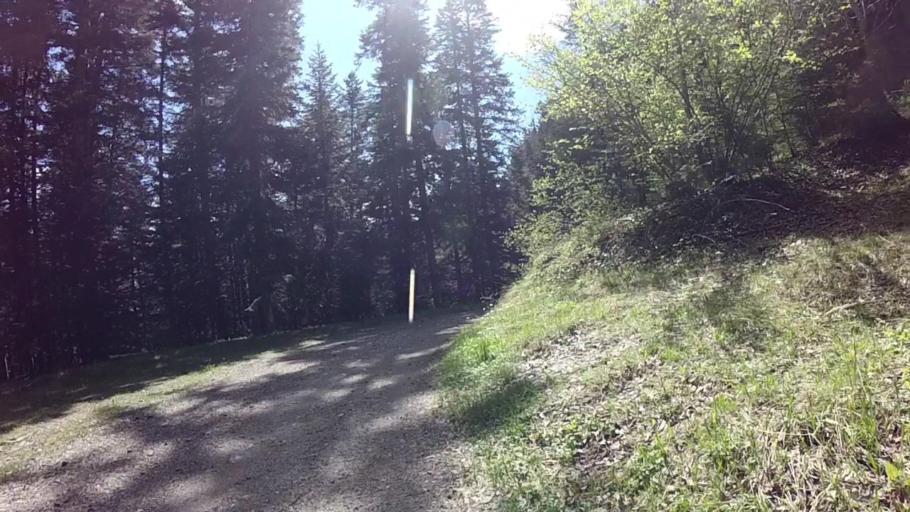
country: FR
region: Provence-Alpes-Cote d'Azur
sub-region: Departement des Alpes-de-Haute-Provence
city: Seyne-les-Alpes
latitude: 44.3334
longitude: 6.3712
